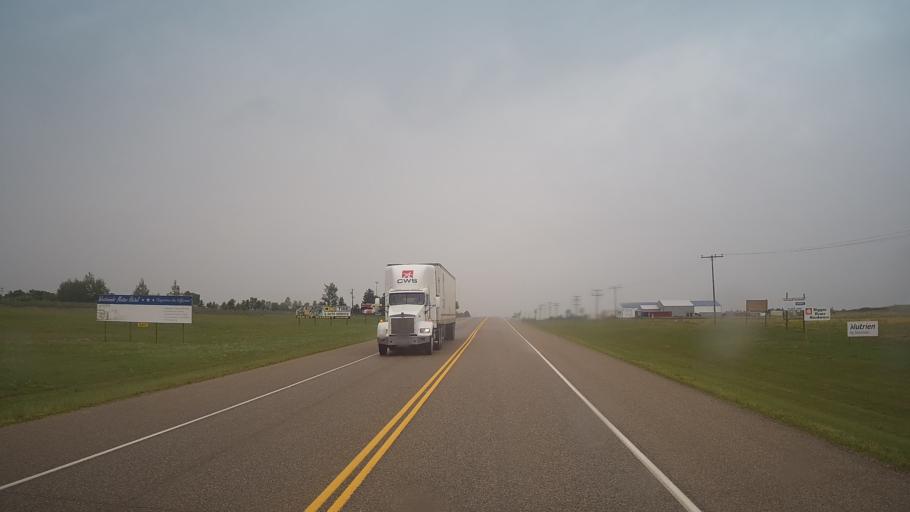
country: CA
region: Saskatchewan
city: Biggar
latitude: 52.0604
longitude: -107.9695
